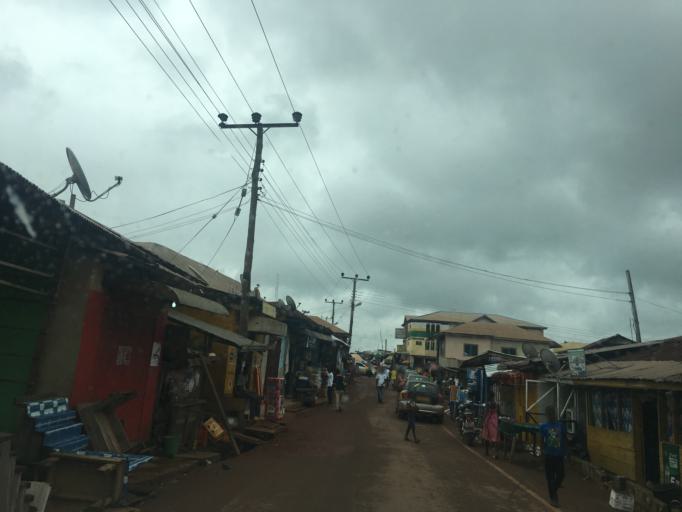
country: GH
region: Western
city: Wassa-Akropong
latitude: 5.8089
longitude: -2.4363
